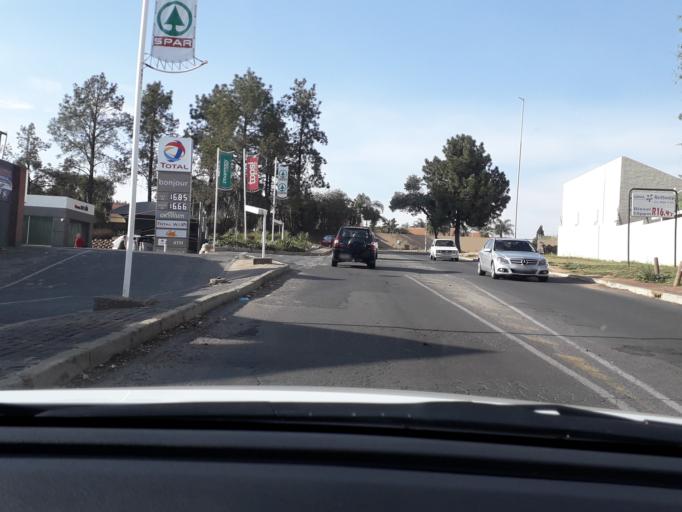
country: ZA
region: Gauteng
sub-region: City of Johannesburg Metropolitan Municipality
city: Roodepoort
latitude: -26.0778
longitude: 27.9454
